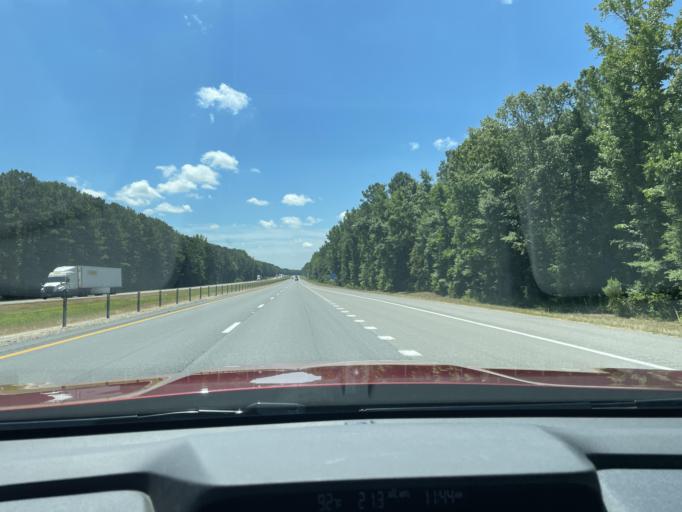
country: US
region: Arkansas
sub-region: Jefferson County
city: White Hall
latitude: 34.3040
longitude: -92.1363
